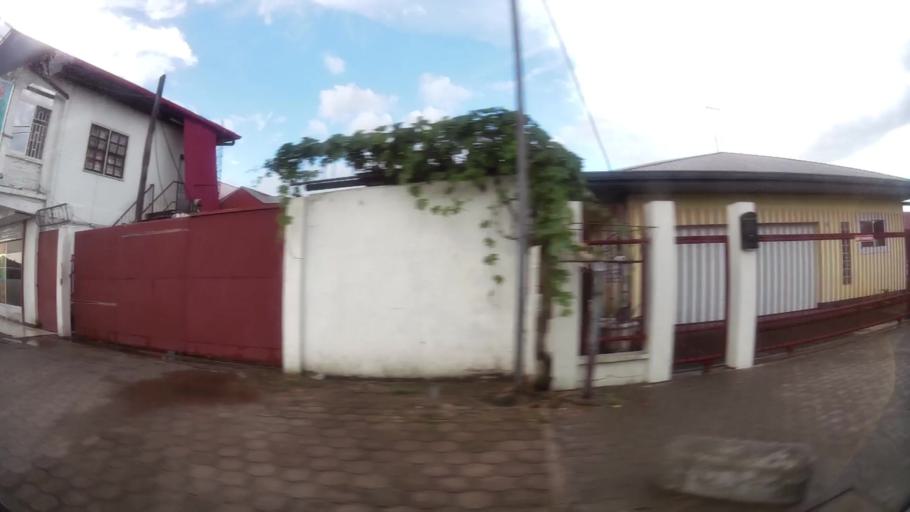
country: SR
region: Paramaribo
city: Paramaribo
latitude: 5.8232
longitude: -55.1740
